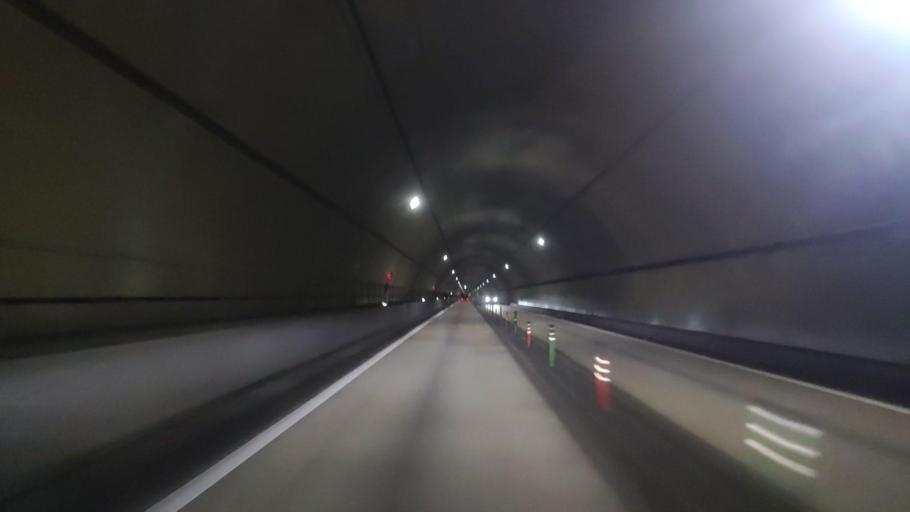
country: JP
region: Wakayama
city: Tanabe
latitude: 33.5439
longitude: 135.5248
